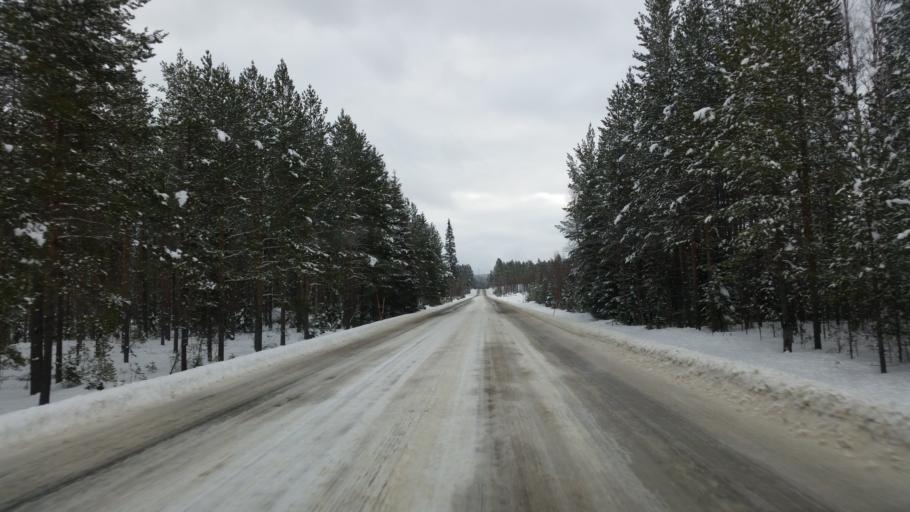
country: SE
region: Gaevleborg
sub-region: Ljusdals Kommun
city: Farila
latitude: 62.0271
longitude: 15.2216
